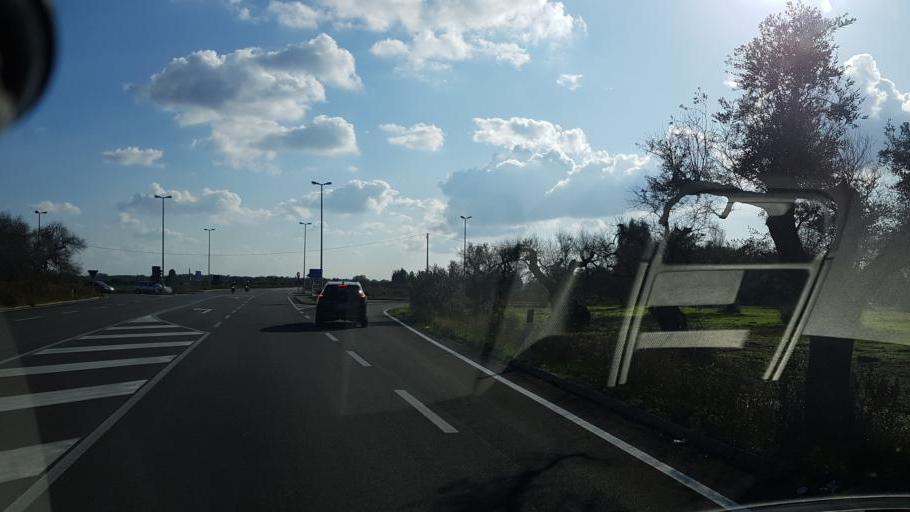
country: IT
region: Apulia
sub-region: Provincia di Lecce
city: Veglie
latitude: 40.3369
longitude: 17.9813
